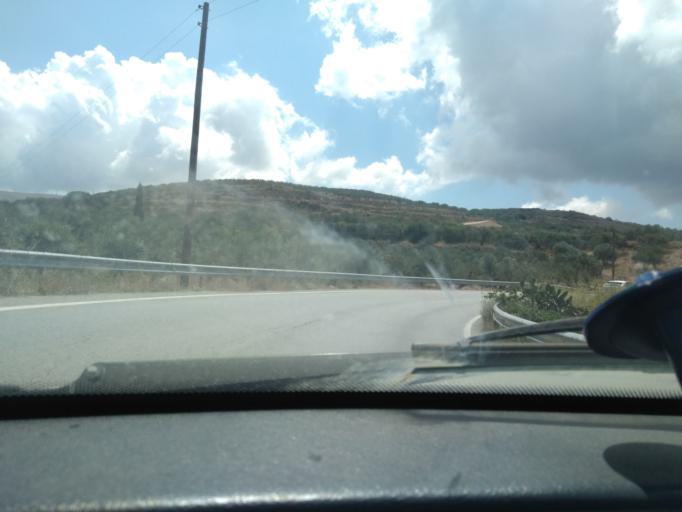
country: GR
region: Crete
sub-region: Nomos Lasithiou
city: Siteia
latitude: 35.1009
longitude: 26.0722
